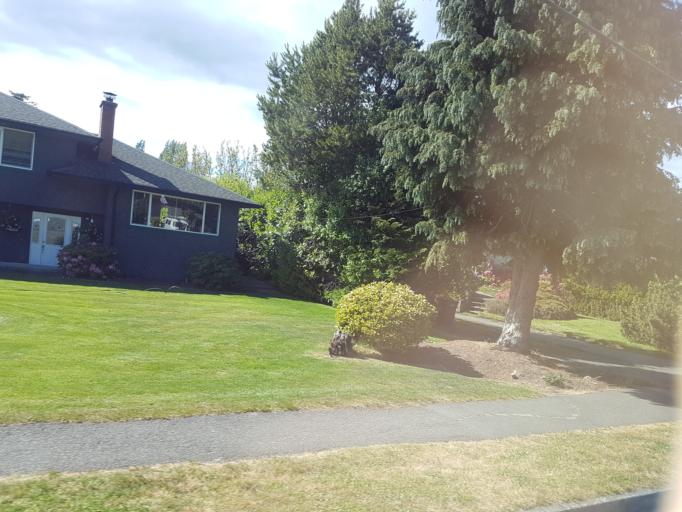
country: CA
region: British Columbia
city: Oak Bay
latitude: 48.4917
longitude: -123.3291
